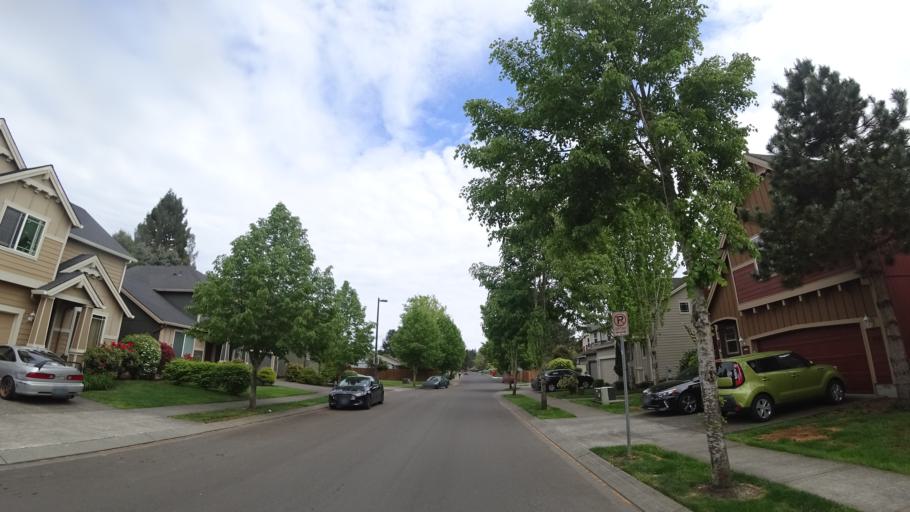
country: US
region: Oregon
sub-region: Washington County
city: Hillsboro
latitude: 45.4948
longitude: -122.9645
